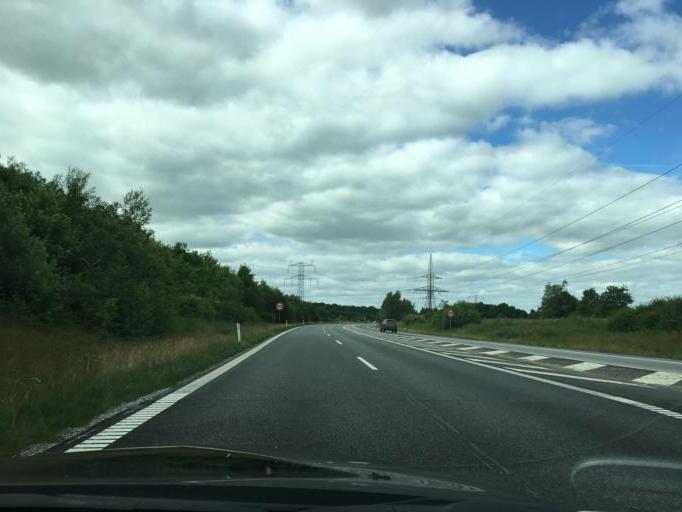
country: DK
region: South Denmark
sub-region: Kolding Kommune
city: Kolding
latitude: 55.5152
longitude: 9.4391
